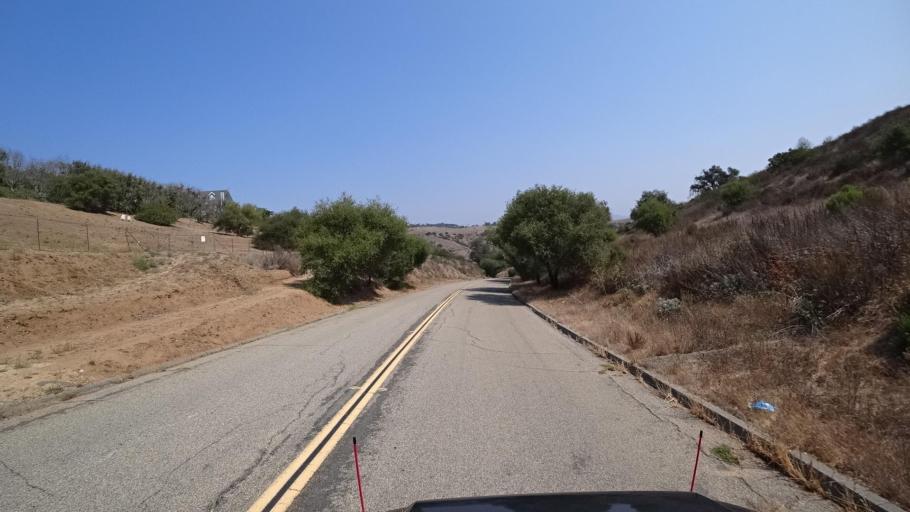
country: US
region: California
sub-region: San Diego County
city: Bonsall
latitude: 33.2904
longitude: -117.2423
